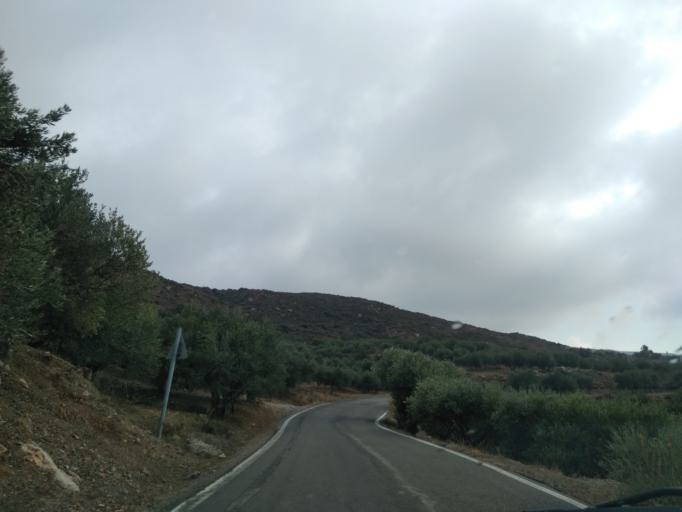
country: GR
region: Crete
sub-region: Nomos Lasithiou
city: Siteia
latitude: 35.1499
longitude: 26.0205
